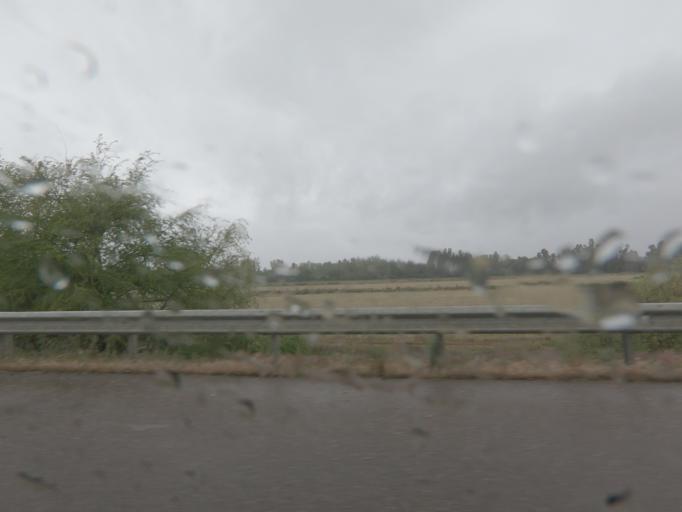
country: ES
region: Extremadura
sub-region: Provincia de Badajoz
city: Badajoz
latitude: 38.9196
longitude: -6.9507
